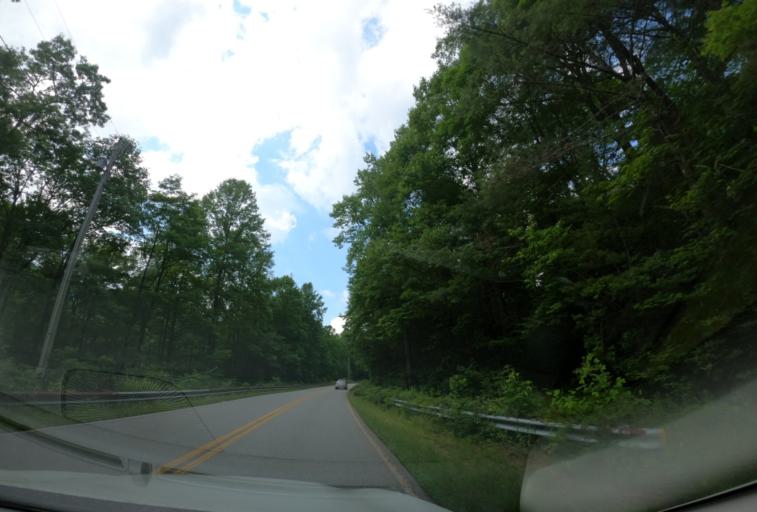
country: US
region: South Carolina
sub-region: Oconee County
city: Walhalla
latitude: 35.0506
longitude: -83.0126
